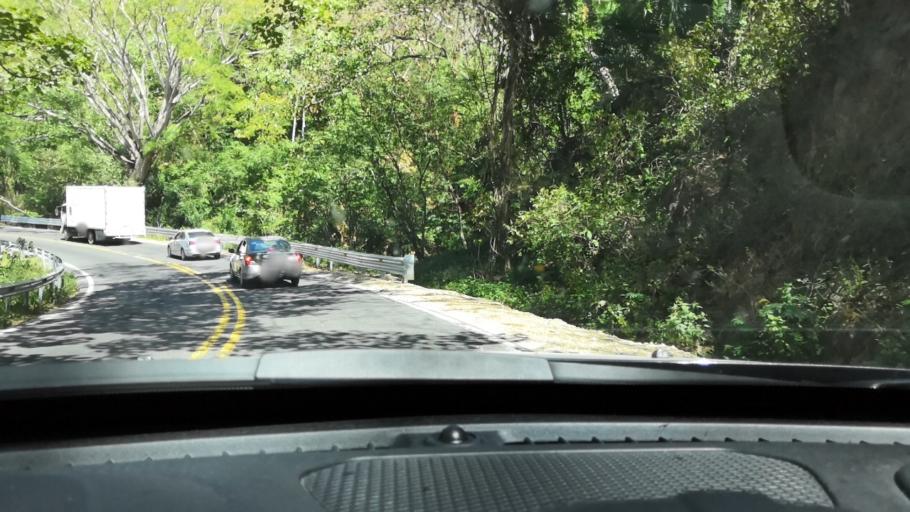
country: MX
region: Nayarit
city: Compostela
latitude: 21.2197
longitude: -104.9972
